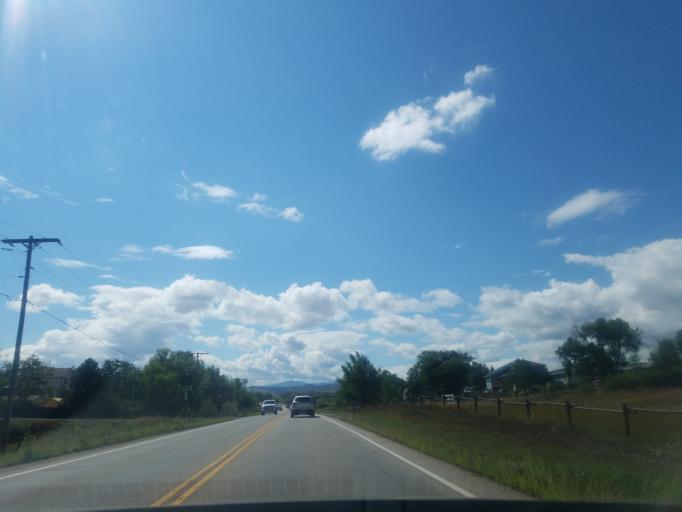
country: US
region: Colorado
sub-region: Larimer County
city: Loveland
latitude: 40.4801
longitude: -105.0672
